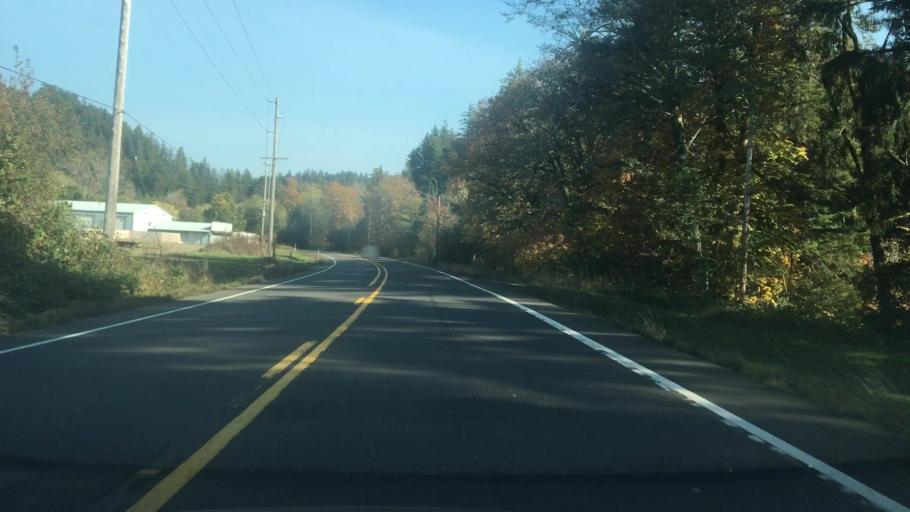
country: US
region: Oregon
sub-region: Lincoln County
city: Rose Lodge
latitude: 45.0225
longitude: -123.8324
